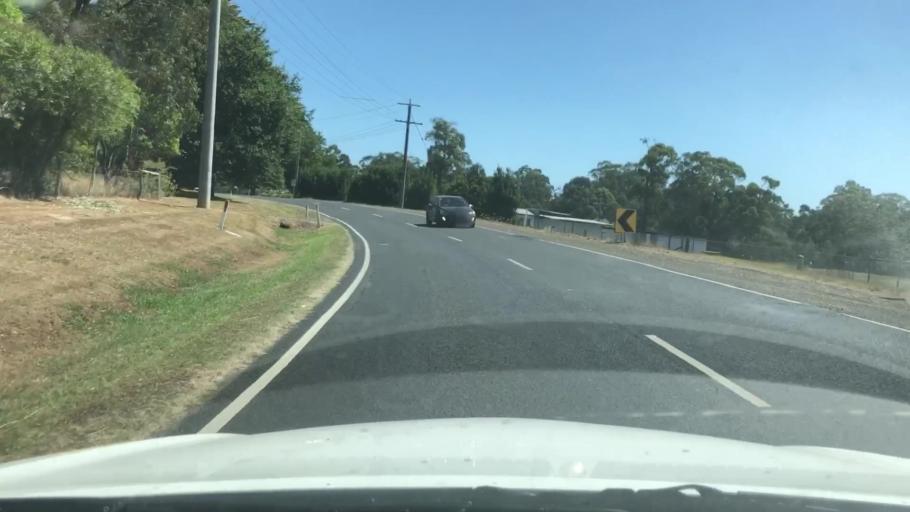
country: AU
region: Victoria
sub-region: Yarra Ranges
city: Woori Yallock
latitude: -37.8090
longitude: 145.5115
